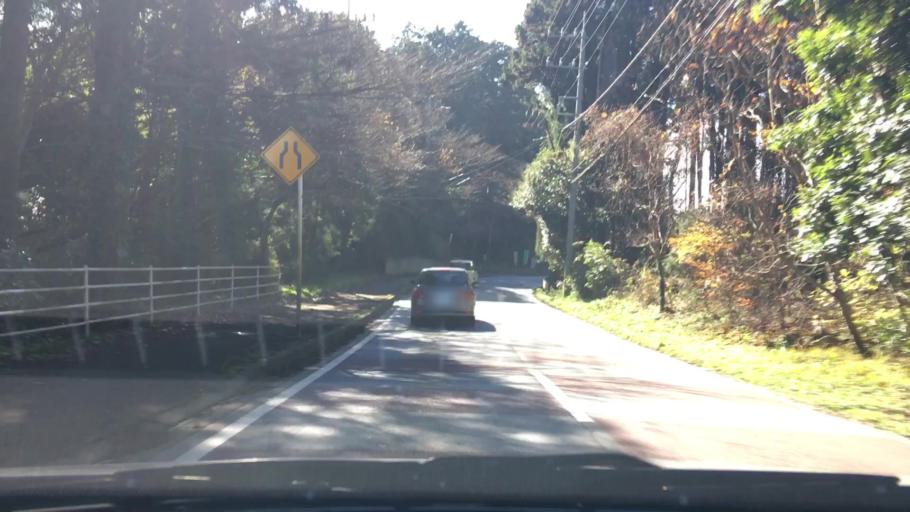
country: JP
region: Chiba
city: Sawara
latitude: 35.8196
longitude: 140.5327
